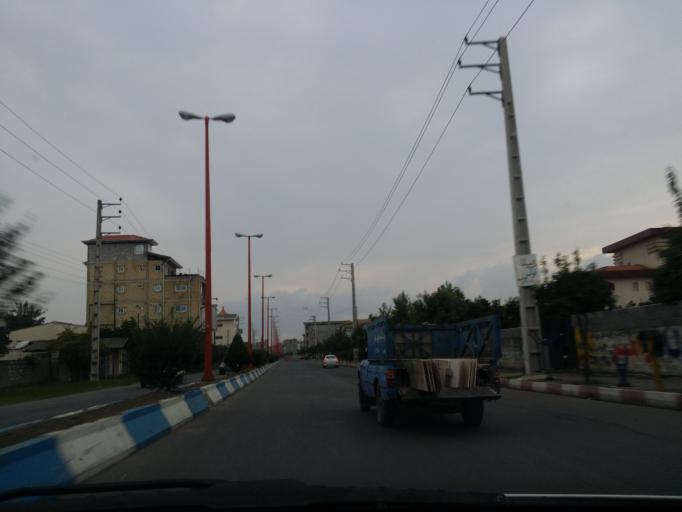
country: IR
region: Mazandaran
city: `Abbasabad
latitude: 36.7148
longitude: 51.1021
